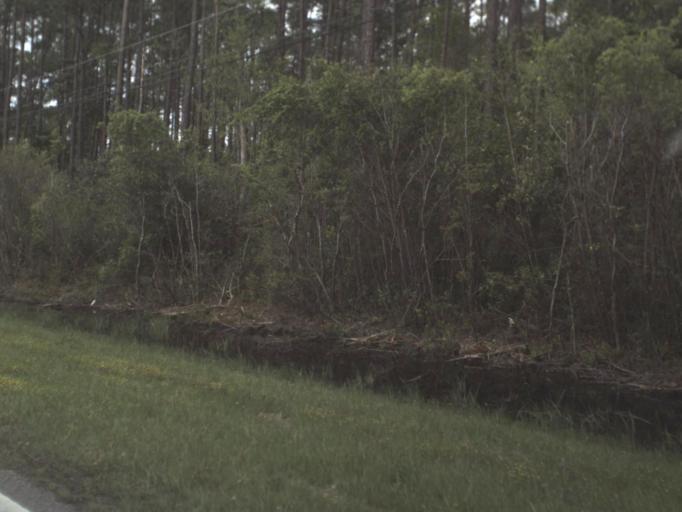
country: US
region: Florida
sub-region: Escambia County
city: Myrtle Grove
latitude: 30.3291
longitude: -87.4151
